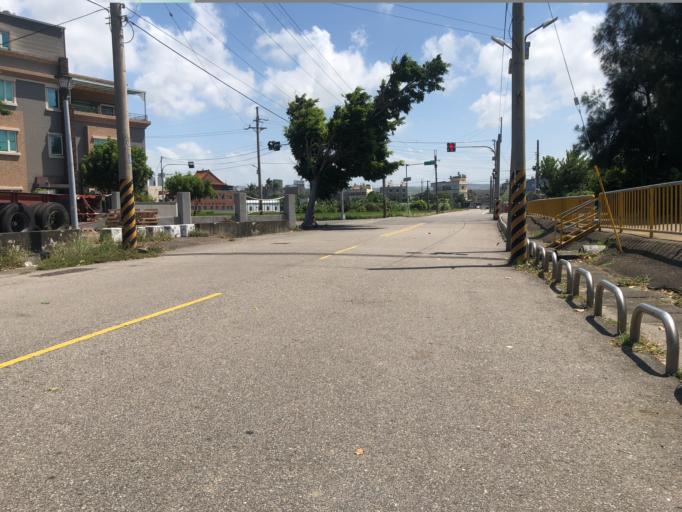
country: TW
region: Taiwan
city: Fengyuan
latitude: 24.2790
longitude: 120.5602
